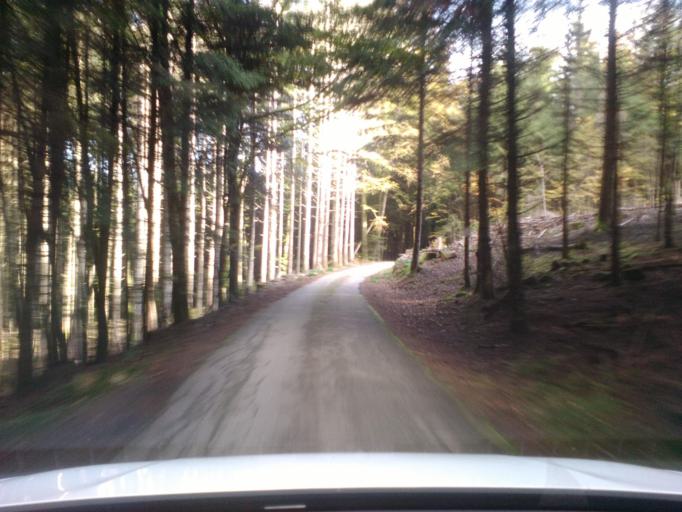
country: FR
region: Lorraine
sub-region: Departement des Vosges
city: Senones
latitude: 48.3964
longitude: 7.0681
